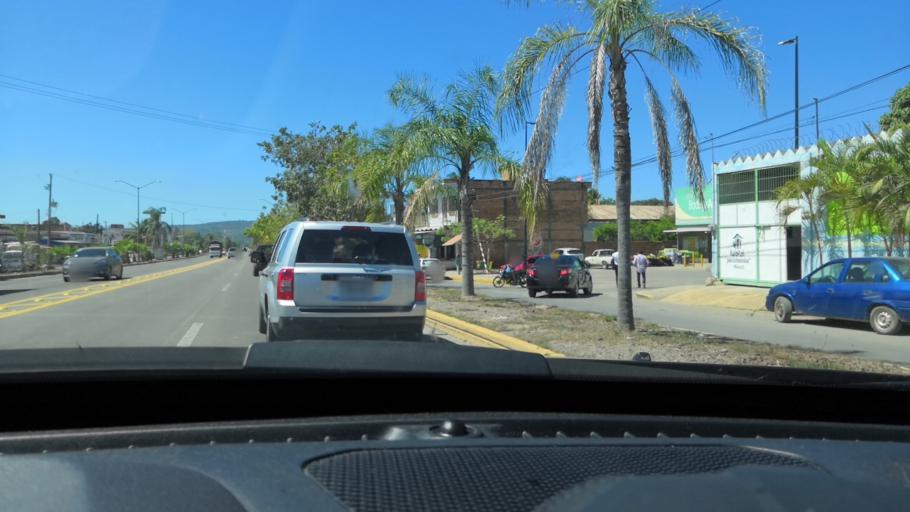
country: MX
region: Nayarit
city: Las Varas
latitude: 21.1829
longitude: -105.1309
